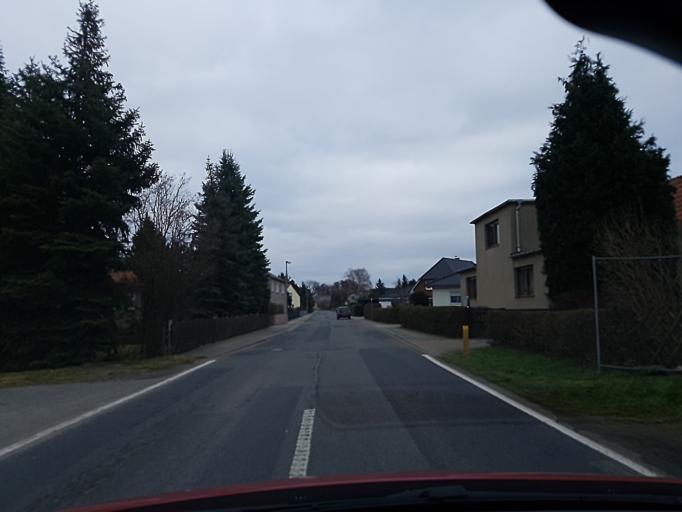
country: DE
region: Brandenburg
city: Merzdorf
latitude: 51.4038
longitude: 13.5286
